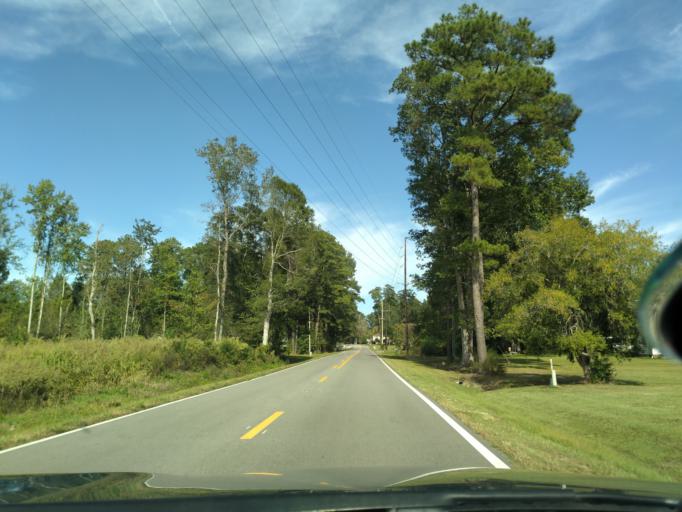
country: US
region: North Carolina
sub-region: Beaufort County
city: River Road
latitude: 35.5185
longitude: -76.9595
